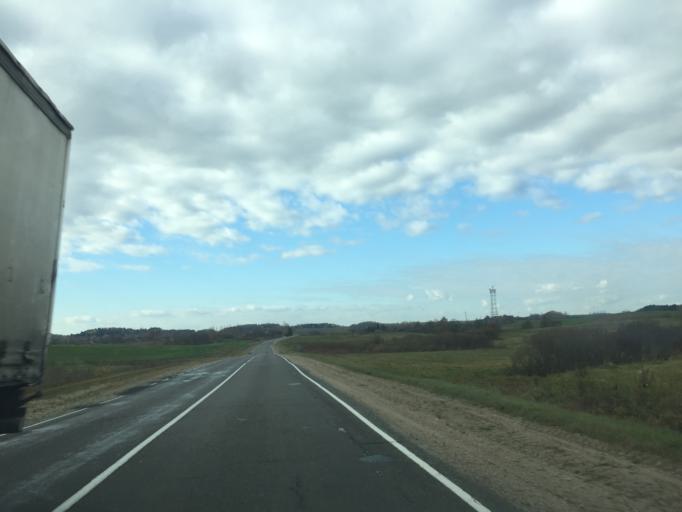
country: BY
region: Vitebsk
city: Mosar
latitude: 55.0615
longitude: 27.2445
